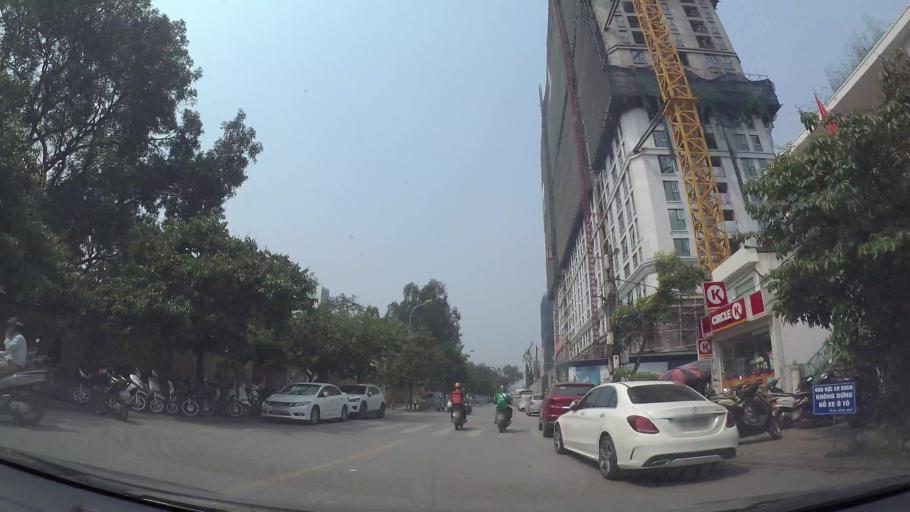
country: VN
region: Ha Noi
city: Dong Da
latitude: 21.0302
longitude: 105.8224
